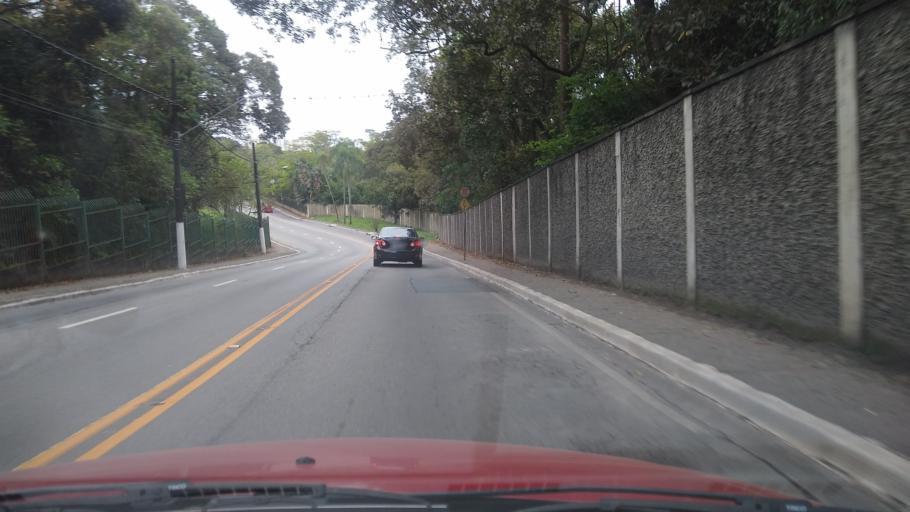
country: BR
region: Sao Paulo
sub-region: Diadema
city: Diadema
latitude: -23.6541
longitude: -46.6172
